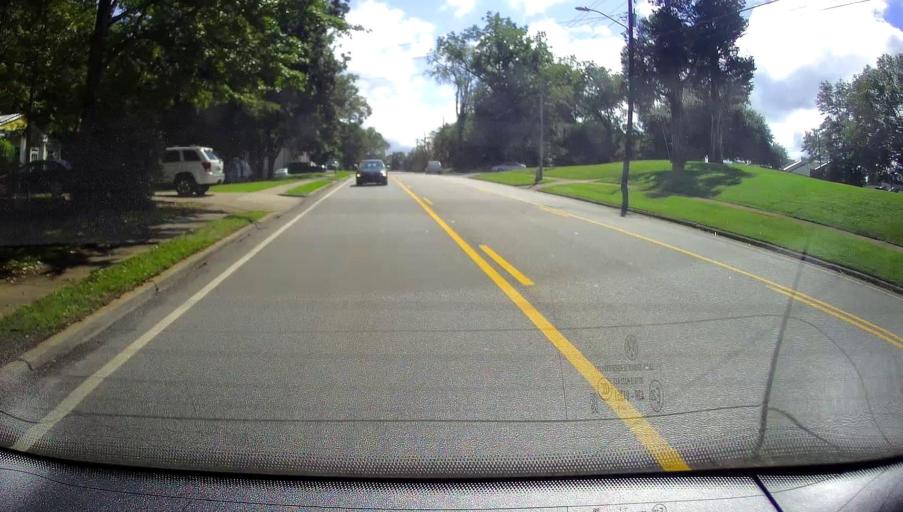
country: US
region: Georgia
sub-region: Baldwin County
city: Milledgeville
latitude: 33.0847
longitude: -83.2350
